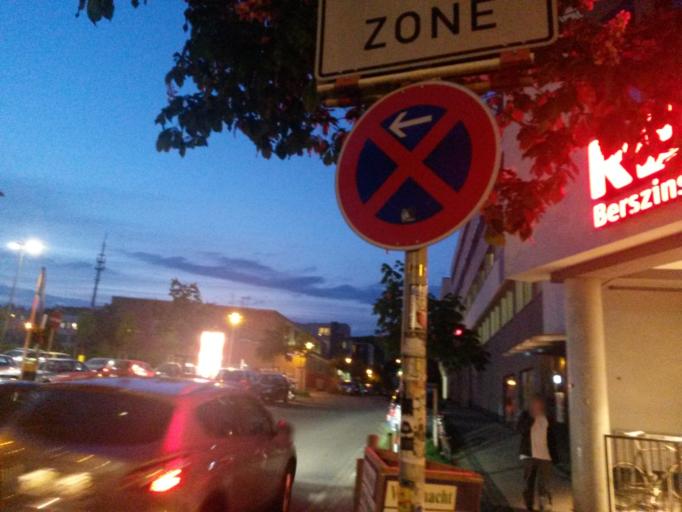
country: DE
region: Hesse
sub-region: Regierungsbezirk Kassel
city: Kassel
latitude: 51.3161
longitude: 9.4724
